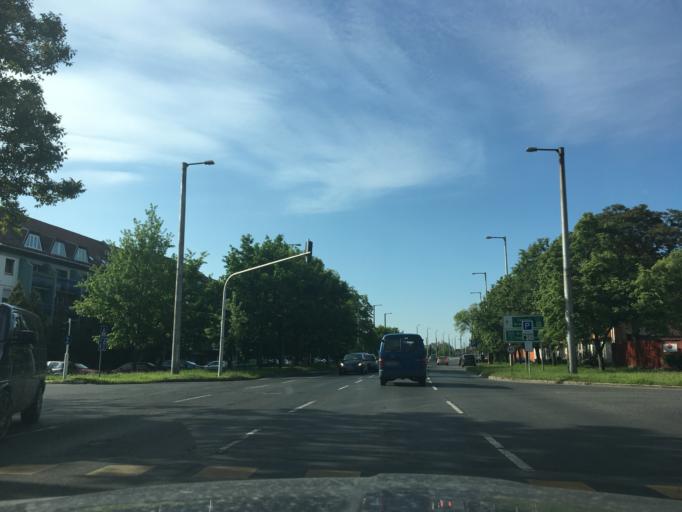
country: HU
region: Hajdu-Bihar
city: Debrecen
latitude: 47.5253
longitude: 21.6325
